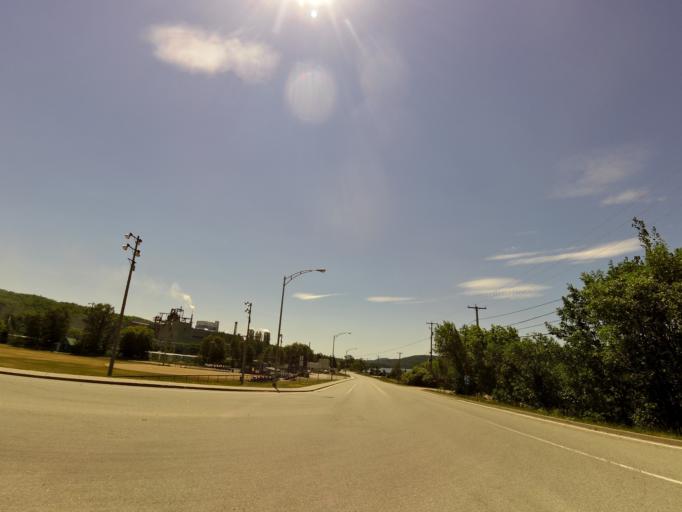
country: CA
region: Quebec
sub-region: Abitibi-Temiscamingue
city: Temiscaming
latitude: 46.7150
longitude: -79.1015
